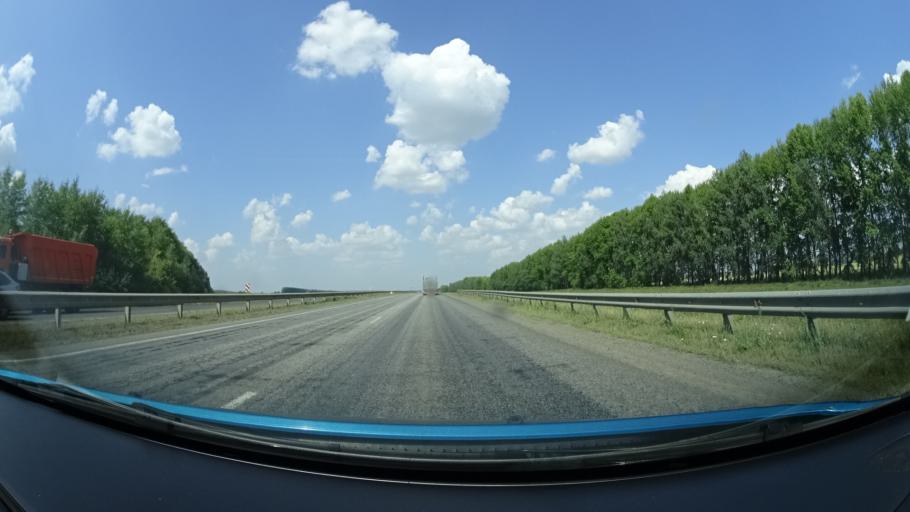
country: RU
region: Bashkortostan
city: Alekseyevka
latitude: 54.7167
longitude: 55.1941
